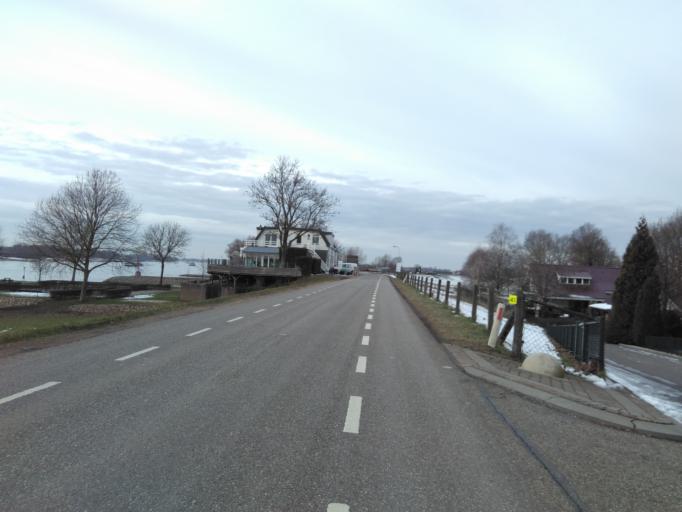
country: NL
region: Gelderland
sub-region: Gemeente Overbetuwe
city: Oosterhout
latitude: 51.8754
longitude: 5.8092
